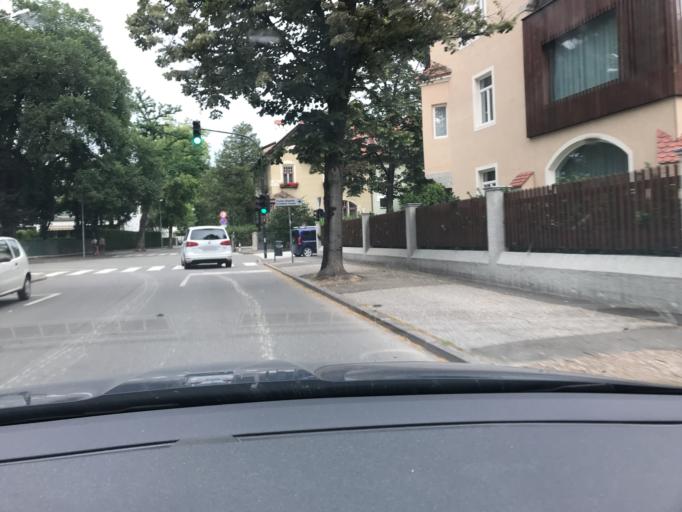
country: IT
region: Trentino-Alto Adige
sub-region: Bolzano
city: Bressanone
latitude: 46.7115
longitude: 11.6557
